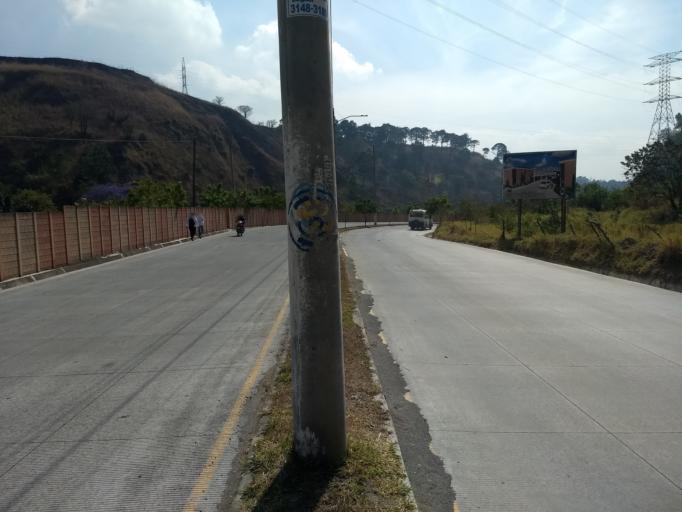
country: GT
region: Guatemala
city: Villa Nueva
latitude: 14.5522
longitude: -90.5901
